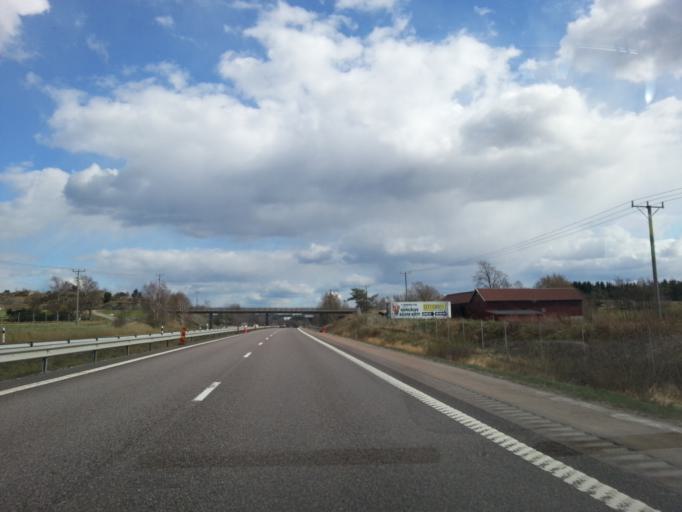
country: SE
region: Vaestra Goetaland
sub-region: Kungalvs Kommun
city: Kungalv
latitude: 57.9004
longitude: 11.9196
